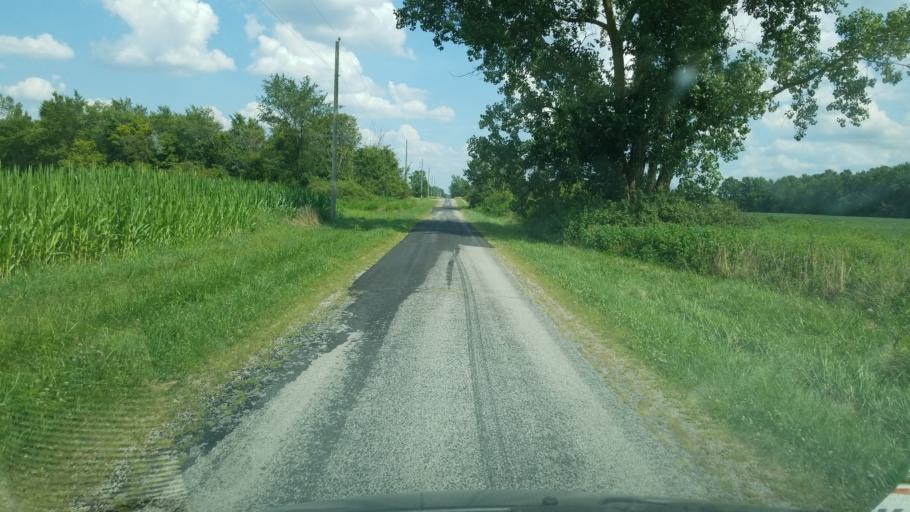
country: US
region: Ohio
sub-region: Union County
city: Richwood
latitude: 40.4000
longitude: -83.4631
